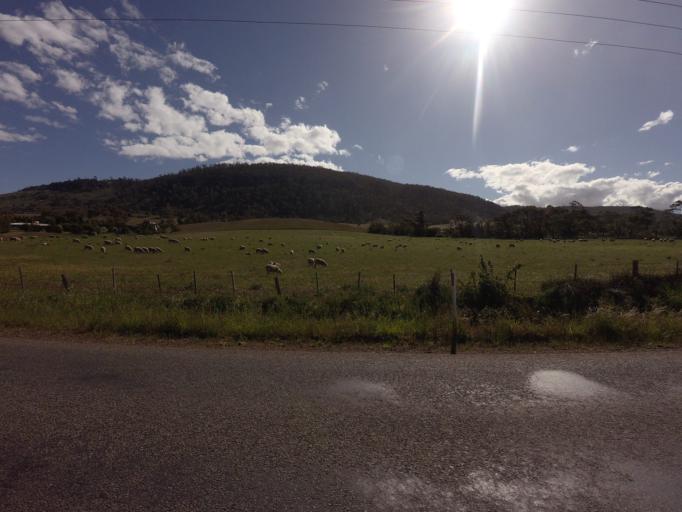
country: AU
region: Tasmania
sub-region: Sorell
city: Sorell
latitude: -42.6303
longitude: 147.4292
